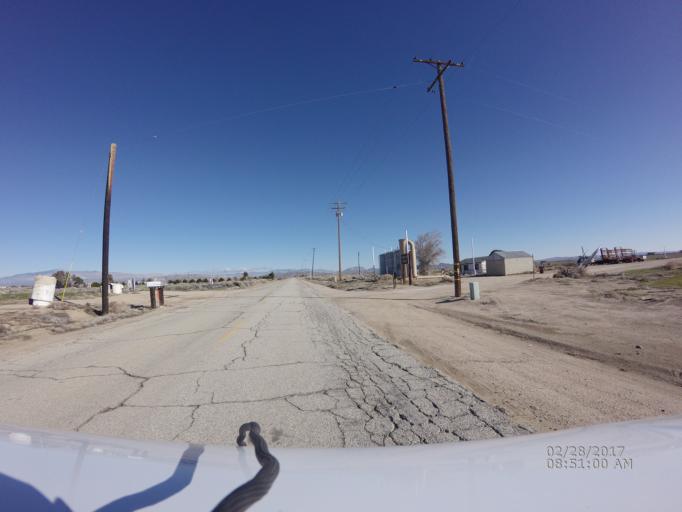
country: US
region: California
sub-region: Kern County
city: Rosamond
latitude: 34.7982
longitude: -118.2376
